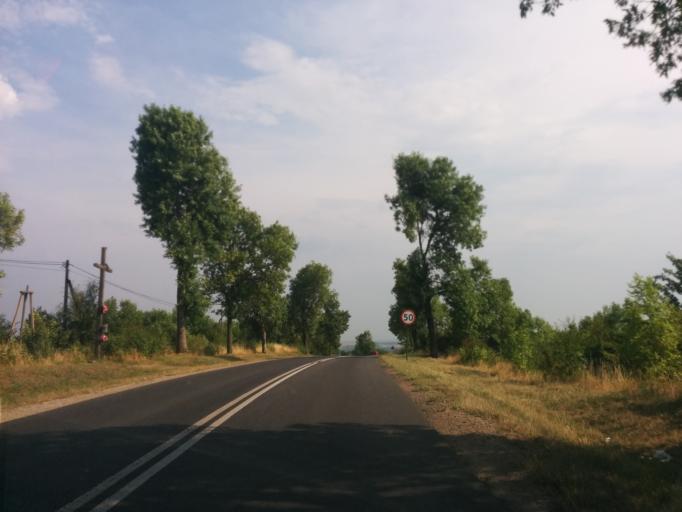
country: PL
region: Silesian Voivodeship
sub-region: Powiat myszkowski
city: Zarki
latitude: 50.6118
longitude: 19.3855
